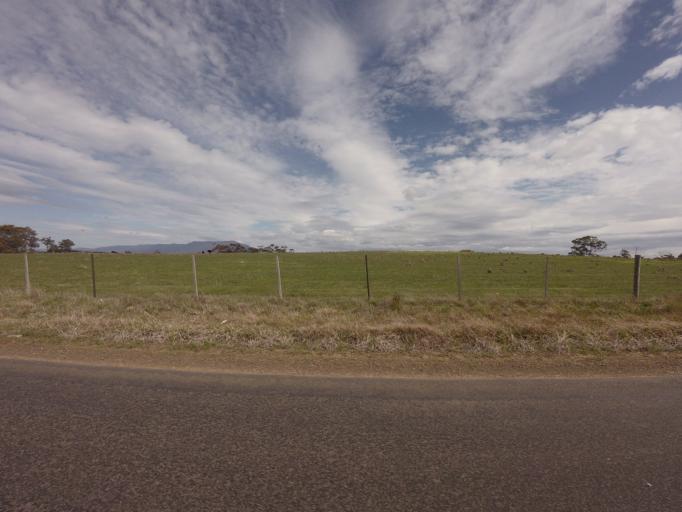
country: AU
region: Tasmania
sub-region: Northern Midlands
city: Longford
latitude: -41.7716
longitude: 147.2198
